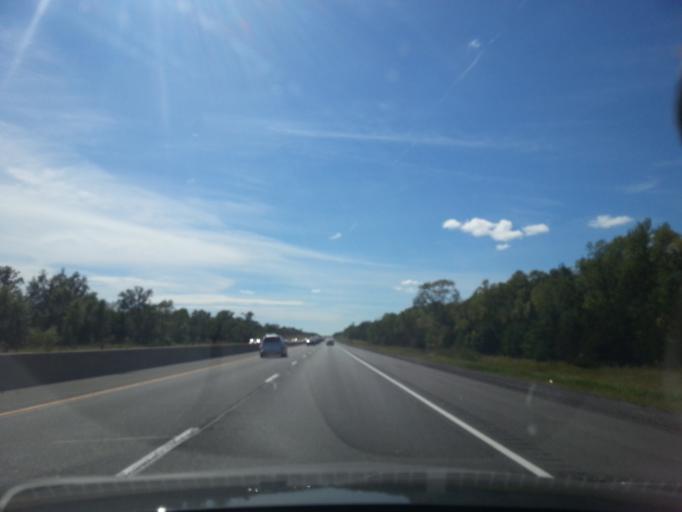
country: CA
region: Ontario
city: Belleville
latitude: 44.2185
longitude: -77.3052
